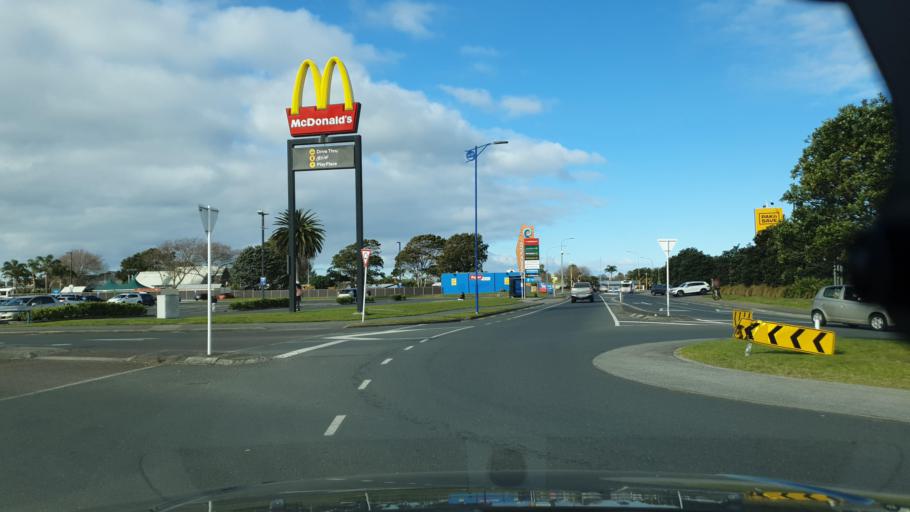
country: NZ
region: Bay of Plenty
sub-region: Tauranga City
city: Tauranga
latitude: -37.7008
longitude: 176.2825
